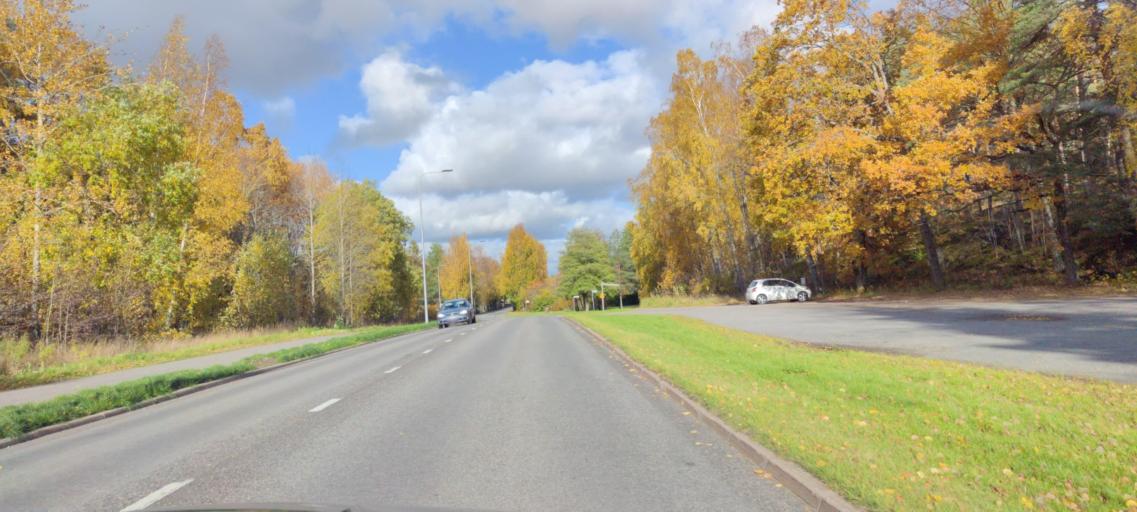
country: FI
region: Varsinais-Suomi
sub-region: Turku
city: Turku
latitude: 60.4171
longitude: 22.2693
